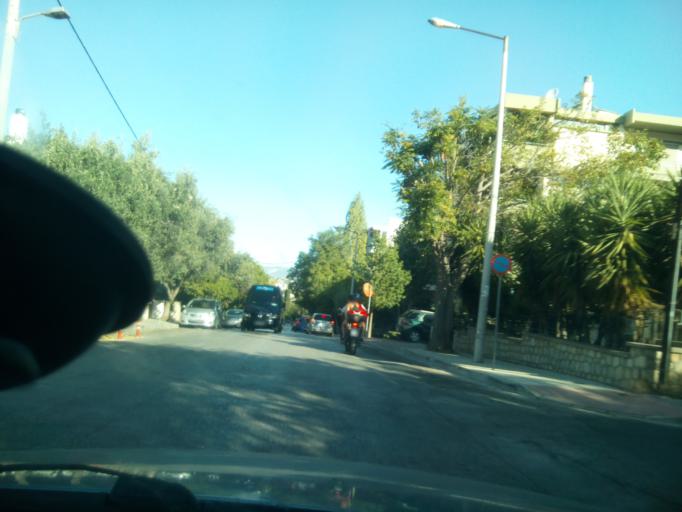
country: GR
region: Attica
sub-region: Nomarchia Athinas
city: Papagou
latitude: 37.9907
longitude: 23.7933
